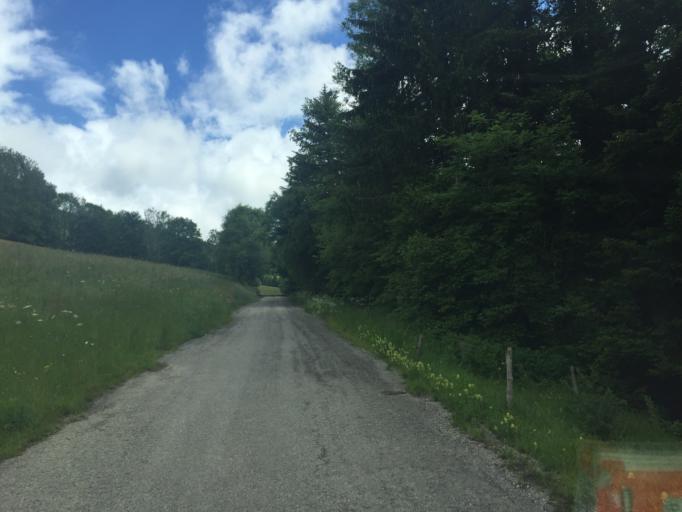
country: FR
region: Rhone-Alpes
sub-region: Departement de la Savoie
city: Cruet
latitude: 45.6193
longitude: 6.1158
